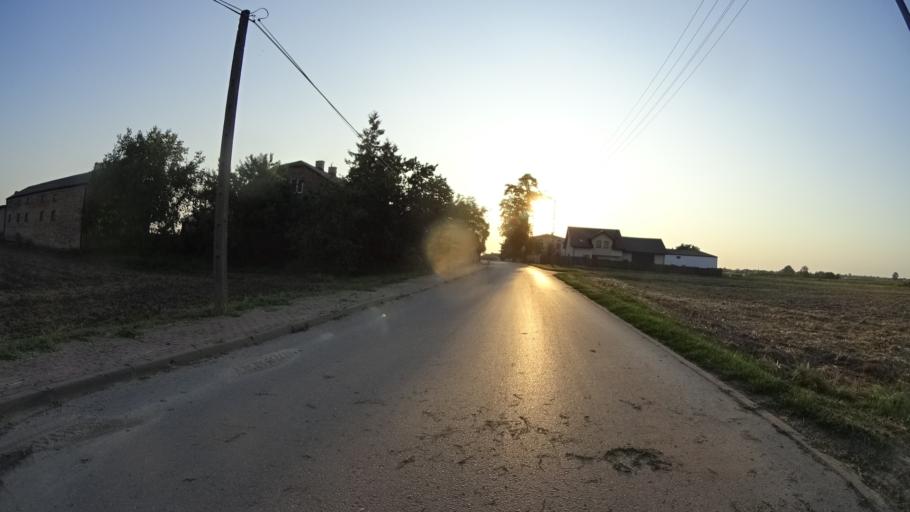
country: PL
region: Masovian Voivodeship
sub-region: Powiat warszawski zachodni
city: Ozarow Mazowiecki
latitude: 52.2409
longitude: 20.7619
